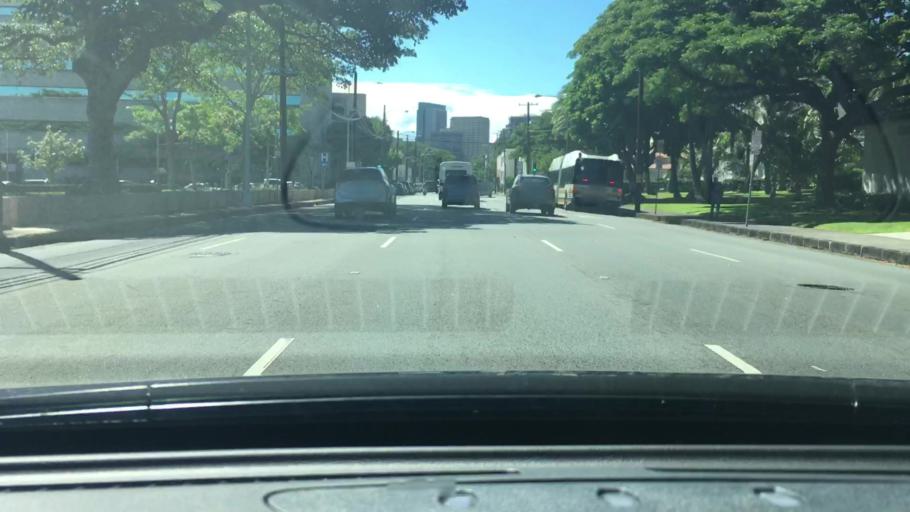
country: US
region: Hawaii
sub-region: Honolulu County
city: Honolulu
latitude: 21.3035
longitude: -157.8486
